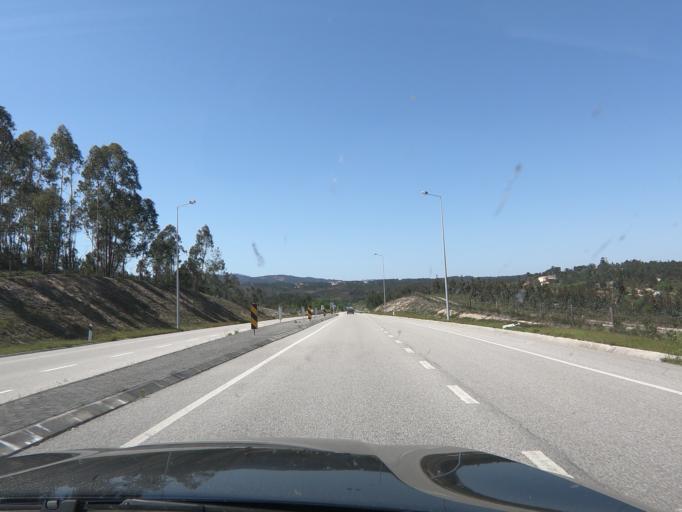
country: PT
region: Coimbra
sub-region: Vila Nova de Poiares
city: Poiares
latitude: 40.1659
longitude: -8.2650
